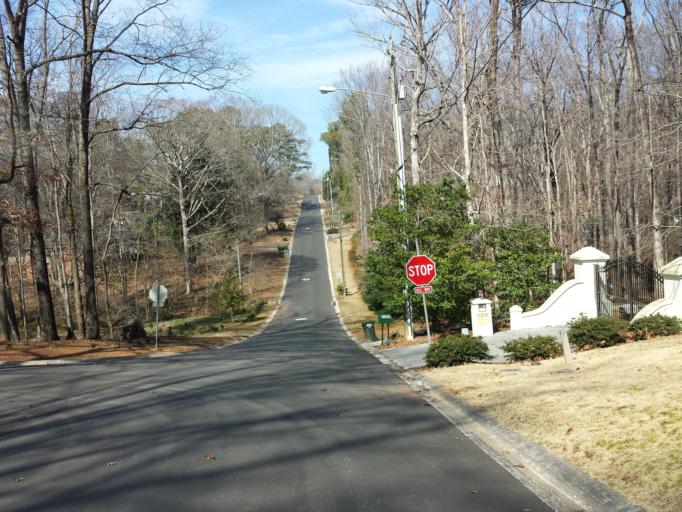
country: US
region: Georgia
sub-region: Cobb County
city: Vinings
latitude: 33.9194
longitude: -84.4581
